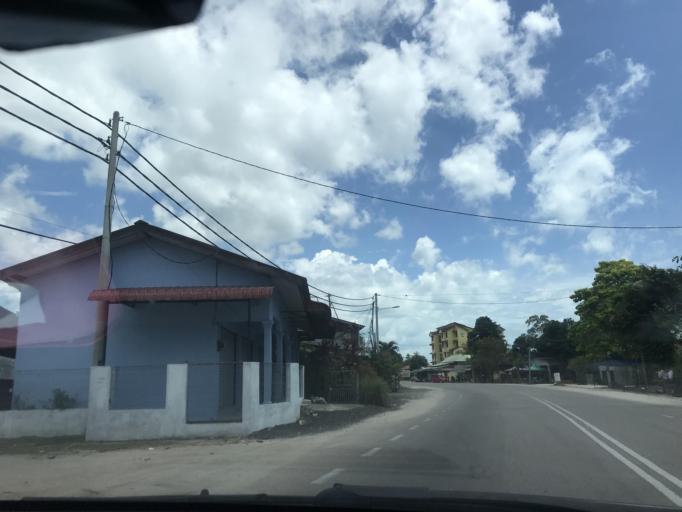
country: TH
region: Narathiwat
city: Tak Bai
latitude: 6.2242
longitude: 102.1054
